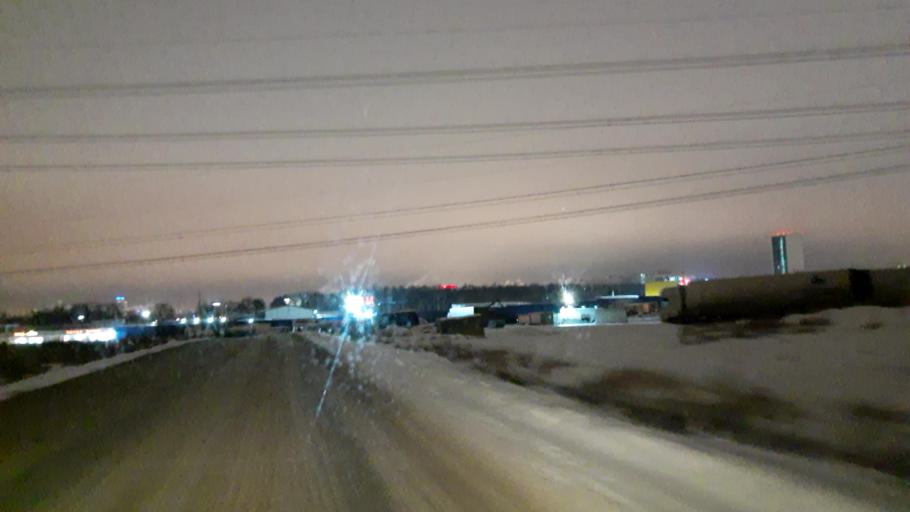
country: RU
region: Moscow
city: Annino
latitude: 55.5698
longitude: 37.6210
